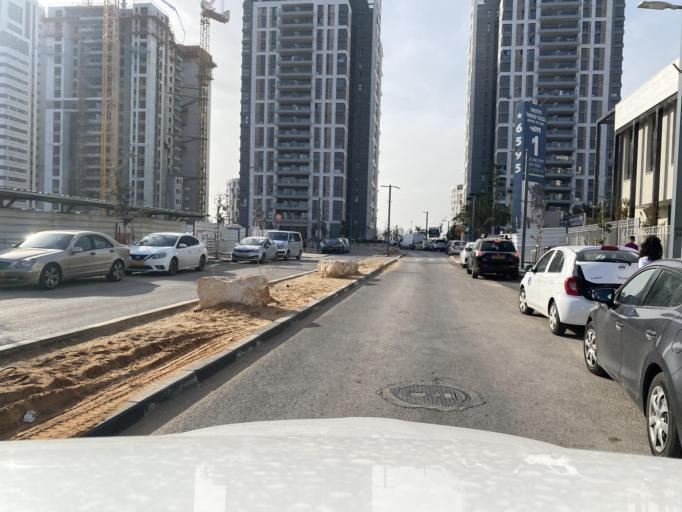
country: IL
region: Tel Aviv
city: Giv`at Shemu'el
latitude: 32.0717
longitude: 34.8530
